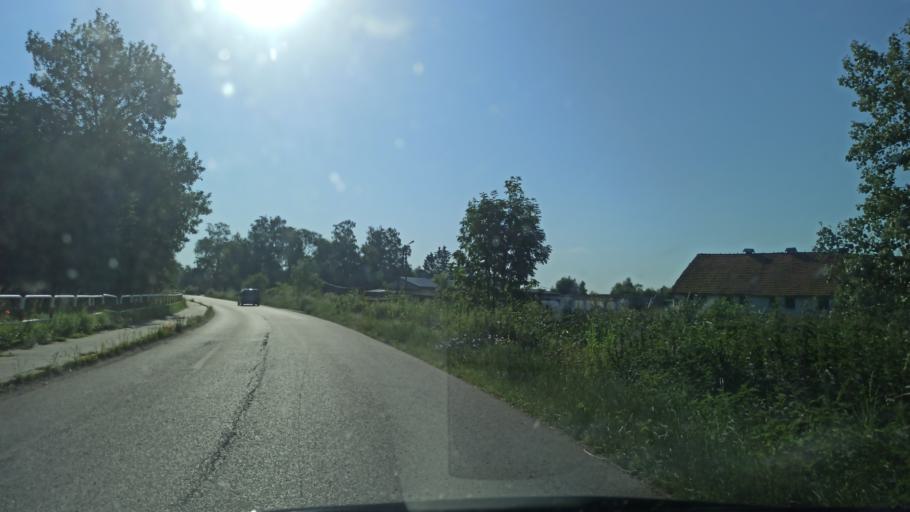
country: PL
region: Warmian-Masurian Voivodeship
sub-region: Powiat elblaski
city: Elblag
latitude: 54.1890
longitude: 19.3230
